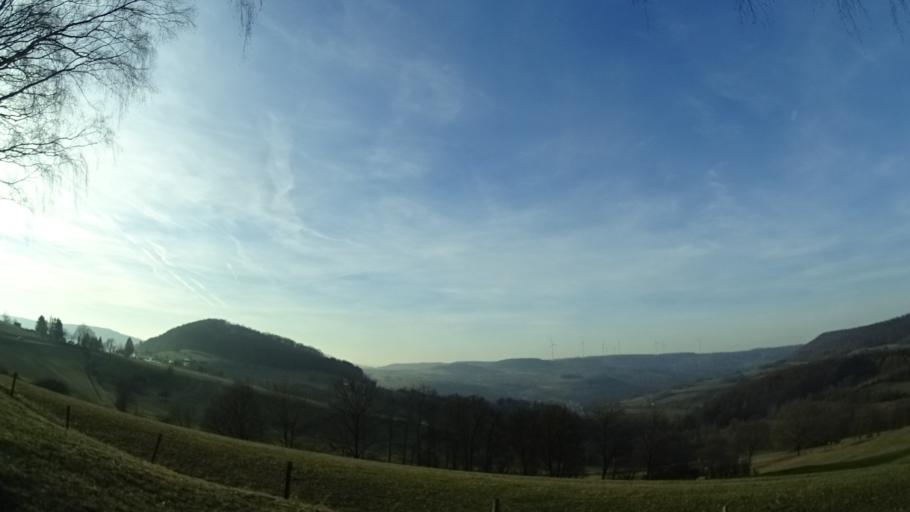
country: DE
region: Bavaria
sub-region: Regierungsbezirk Unterfranken
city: Zeitlofs
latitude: 50.3011
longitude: 9.6917
